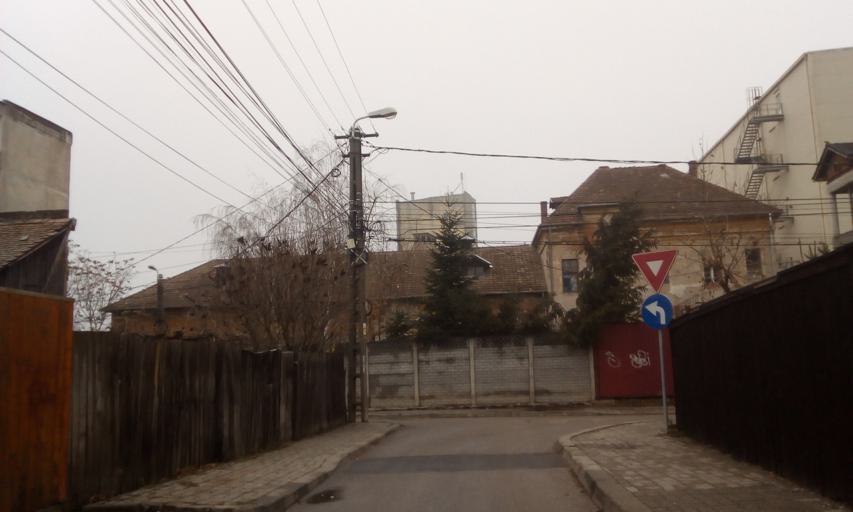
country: RO
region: Timis
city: Timisoara
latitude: 45.7506
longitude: 21.2474
